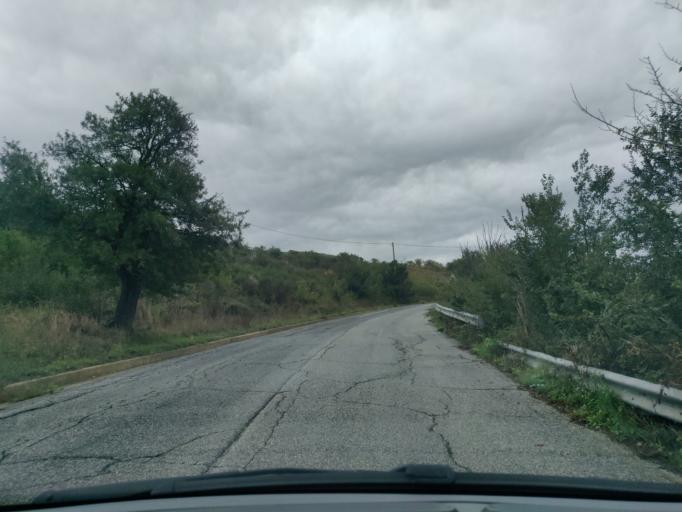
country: IT
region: Latium
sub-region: Citta metropolitana di Roma Capitale
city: Aurelia
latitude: 42.1308
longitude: 11.8463
